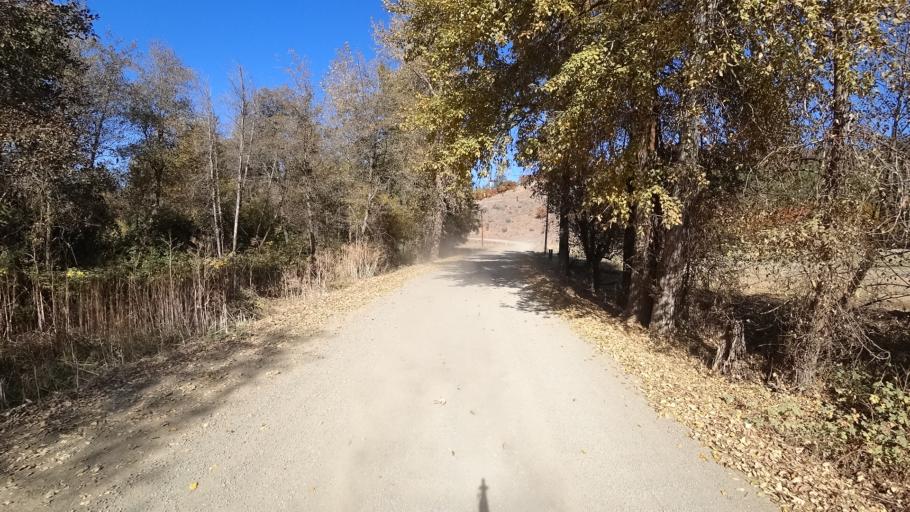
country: US
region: California
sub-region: Siskiyou County
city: Yreka
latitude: 41.6041
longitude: -122.9600
